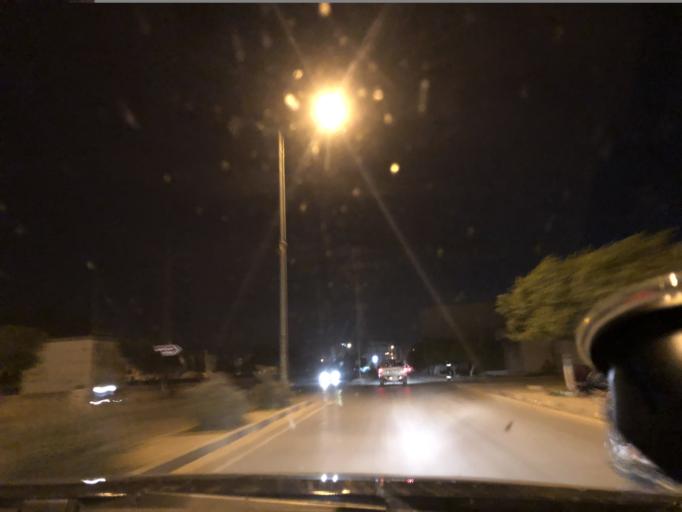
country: TN
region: Al Qasrayn
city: Kasserine
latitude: 35.1752
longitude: 8.8483
